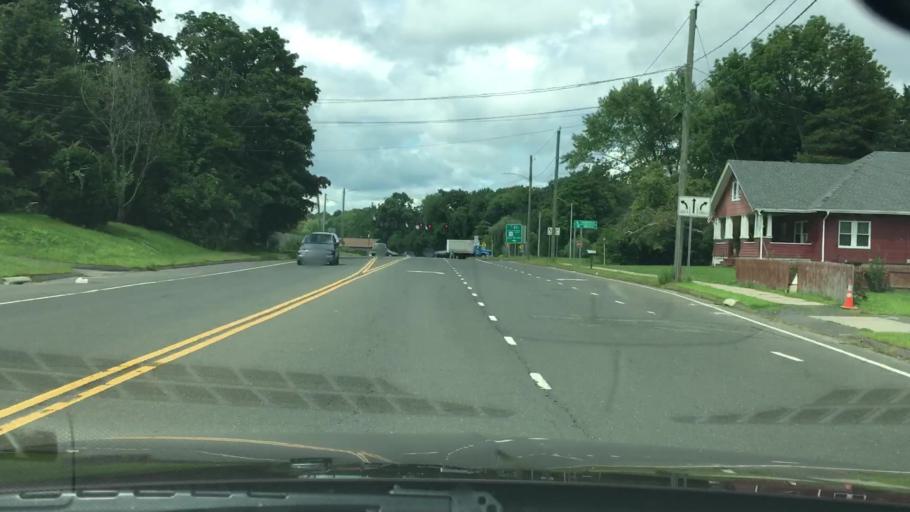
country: US
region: Connecticut
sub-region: Hartford County
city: Plainville
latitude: 41.6718
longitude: -72.8842
